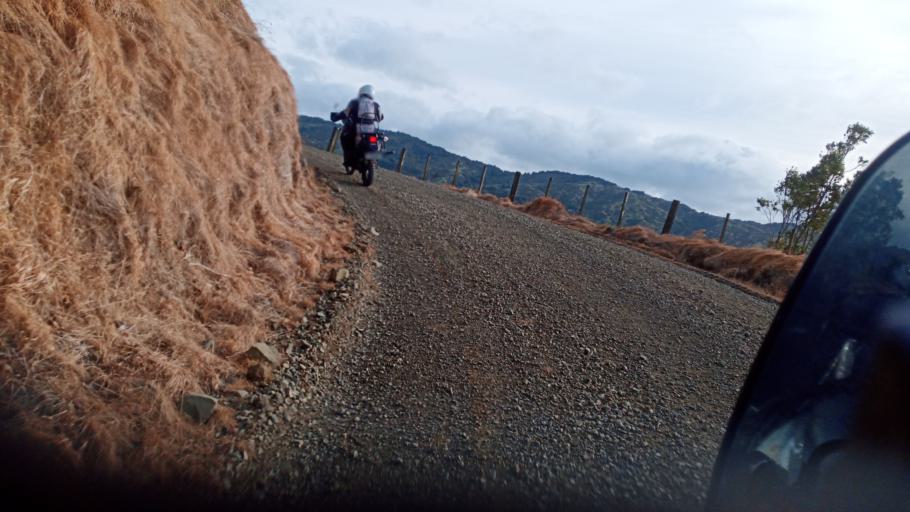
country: NZ
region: Gisborne
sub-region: Gisborne District
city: Gisborne
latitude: -38.4623
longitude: 177.5367
